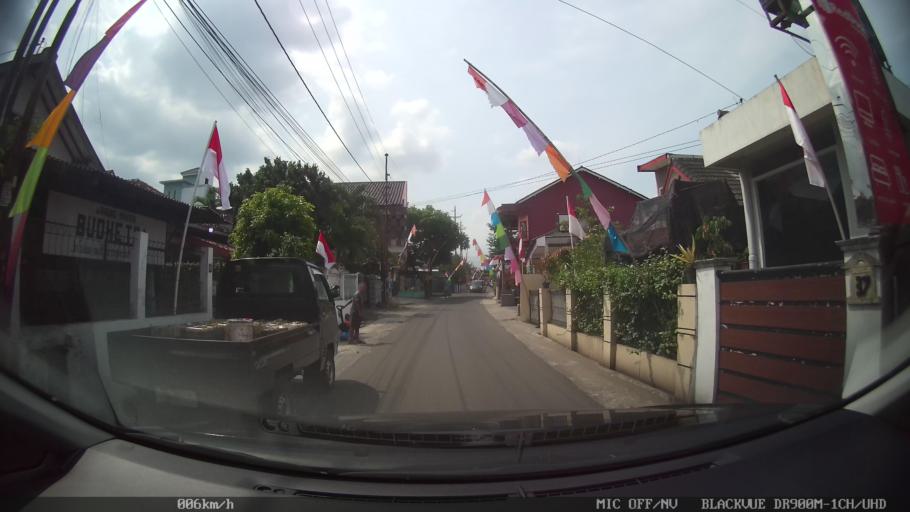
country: ID
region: Daerah Istimewa Yogyakarta
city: Depok
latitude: -7.7886
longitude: 110.4053
